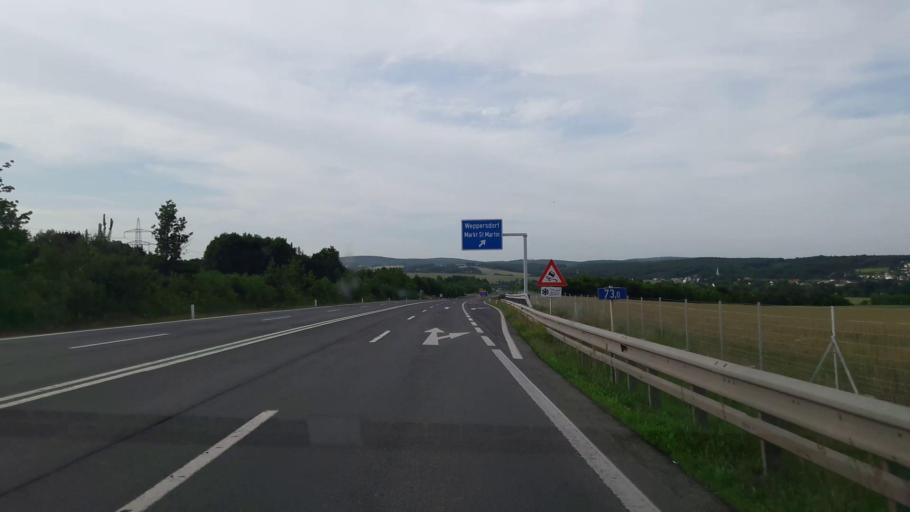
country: AT
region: Burgenland
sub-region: Politischer Bezirk Oberpullendorf
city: Markt Sankt Martin
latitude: 47.5678
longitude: 16.4158
